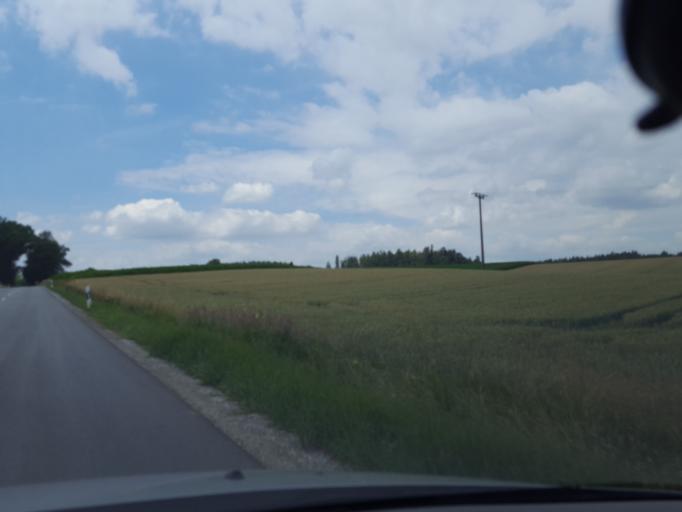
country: DE
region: Bavaria
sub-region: Lower Bavaria
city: Schalkham
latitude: 48.4469
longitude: 12.4065
